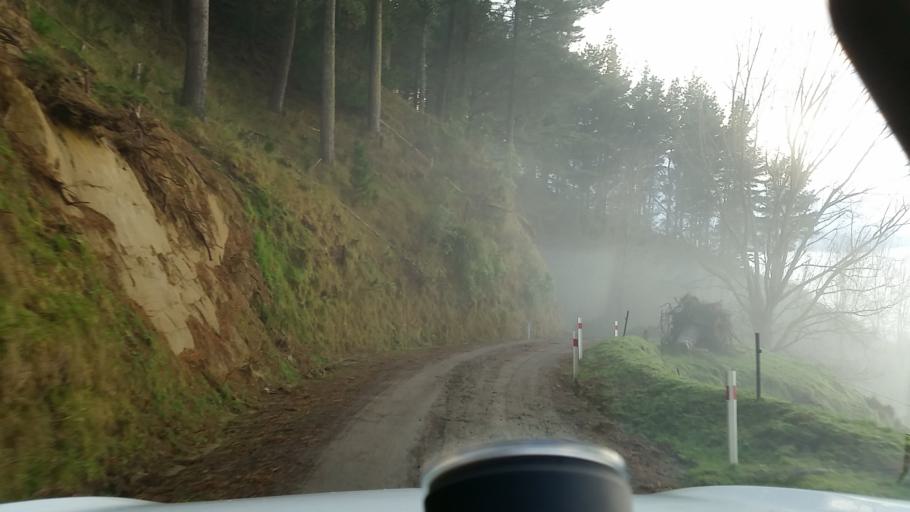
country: NZ
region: Taranaki
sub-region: South Taranaki District
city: Eltham
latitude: -39.4492
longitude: 174.4578
